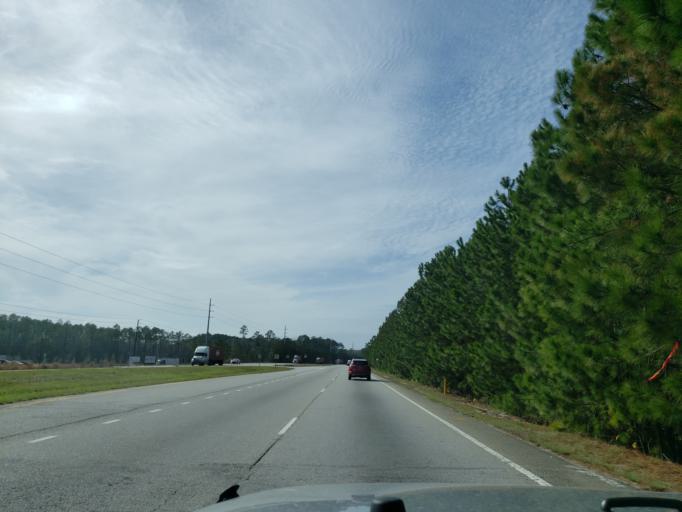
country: US
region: Georgia
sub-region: Chatham County
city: Pooler
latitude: 32.1667
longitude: -81.2248
